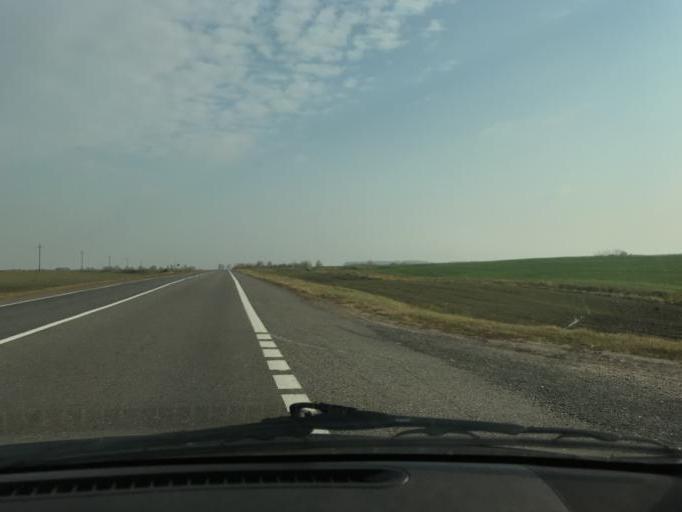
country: BY
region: Vitebsk
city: Chashniki
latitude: 55.0139
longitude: 29.0024
